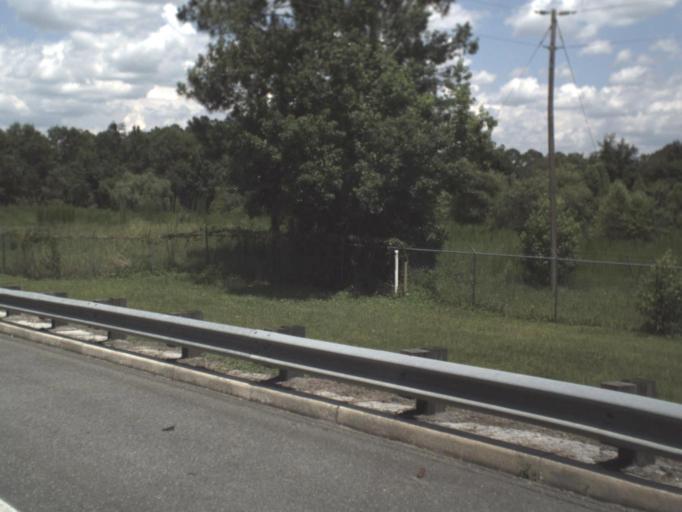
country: US
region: Florida
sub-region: Columbia County
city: Lake City
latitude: 30.1664
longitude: -82.6794
